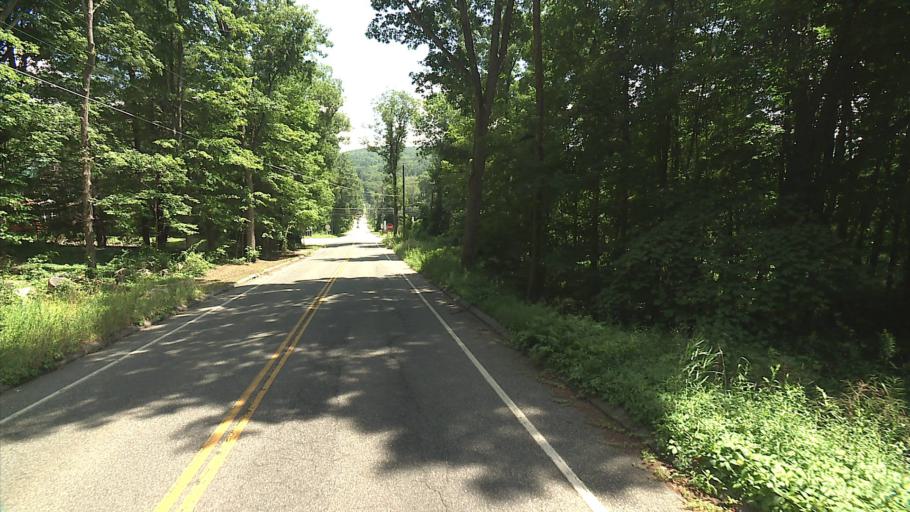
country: US
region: Connecticut
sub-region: Litchfield County
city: Litchfield
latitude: 41.8488
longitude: -73.3125
